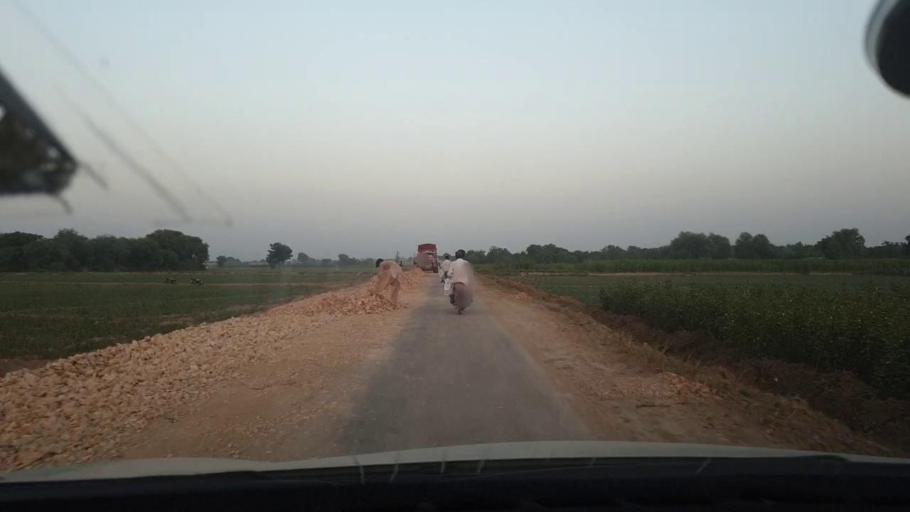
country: PK
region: Sindh
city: Bhit Shah
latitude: 25.7528
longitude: 68.5390
